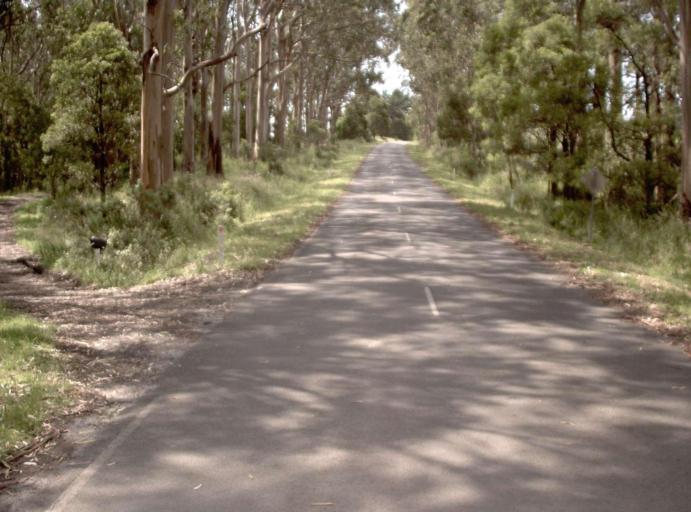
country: AU
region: Victoria
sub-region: Latrobe
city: Traralgon
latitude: -38.3643
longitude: 146.7027
